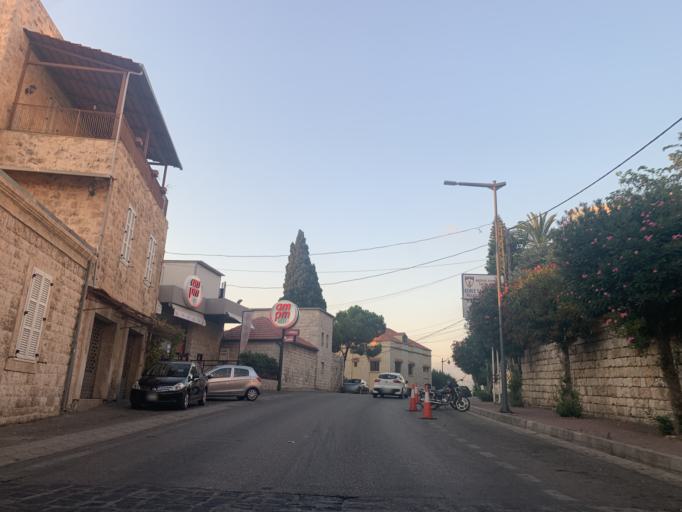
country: LB
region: Mont-Liban
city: Djounie
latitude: 33.9653
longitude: 35.6253
